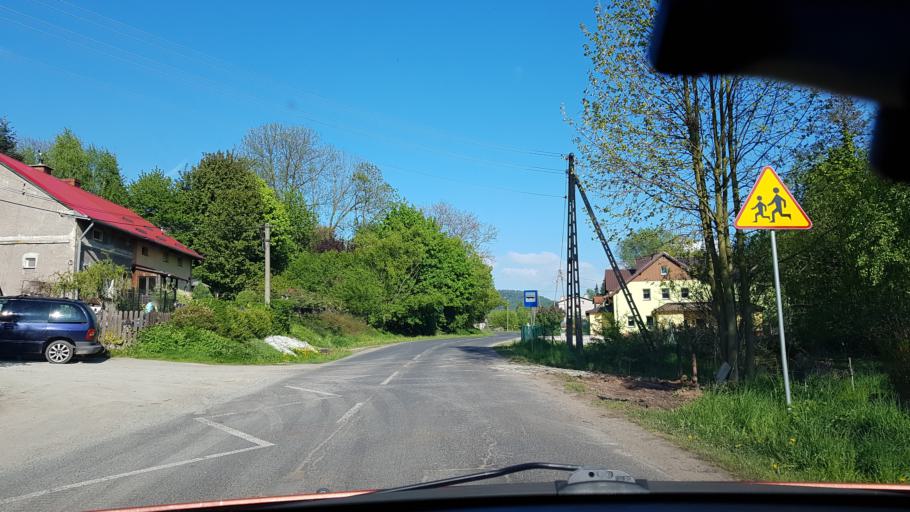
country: PL
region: Lower Silesian Voivodeship
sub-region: Powiat klodzki
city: Nowa Ruda
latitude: 50.5896
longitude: 16.5486
